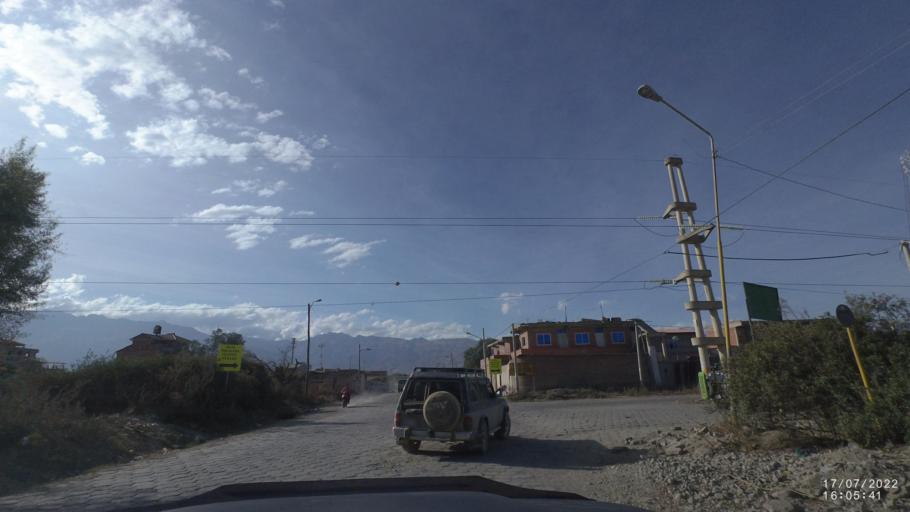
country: BO
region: Cochabamba
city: Sipe Sipe
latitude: -17.4151
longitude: -66.2815
